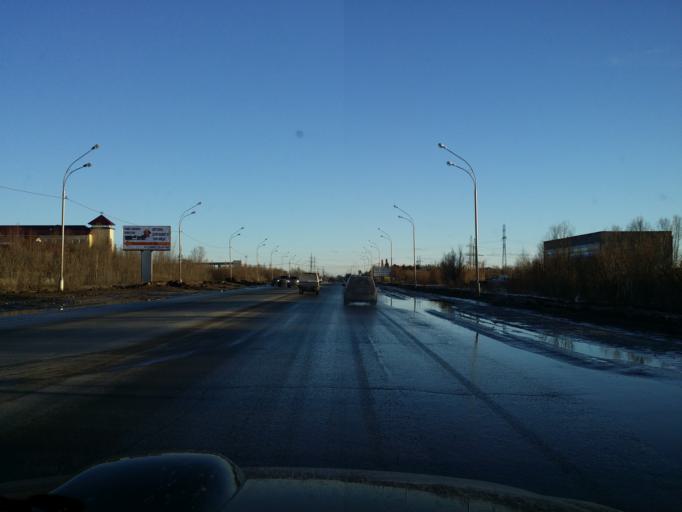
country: RU
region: Khanty-Mansiyskiy Avtonomnyy Okrug
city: Nizhnevartovsk
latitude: 60.9623
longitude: 76.5304
